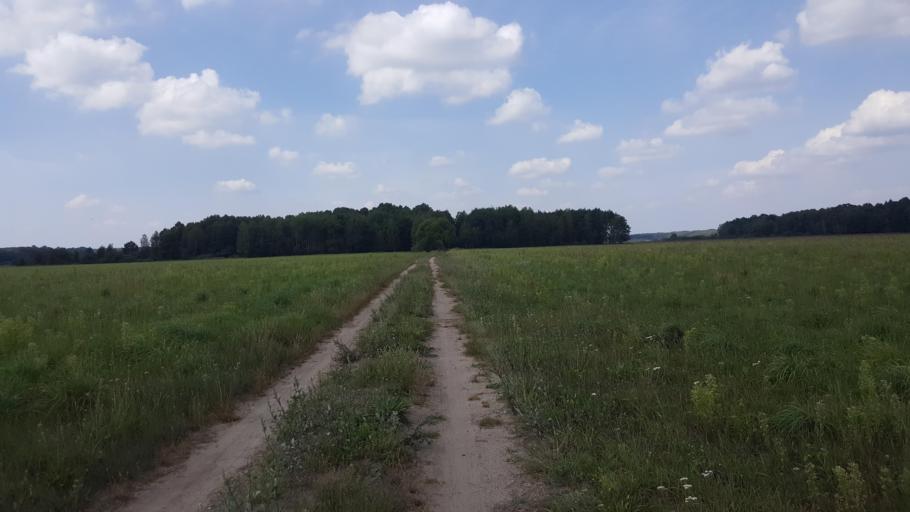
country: PL
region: Podlasie
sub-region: Powiat hajnowski
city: Hajnowka
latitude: 52.5698
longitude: 23.6000
